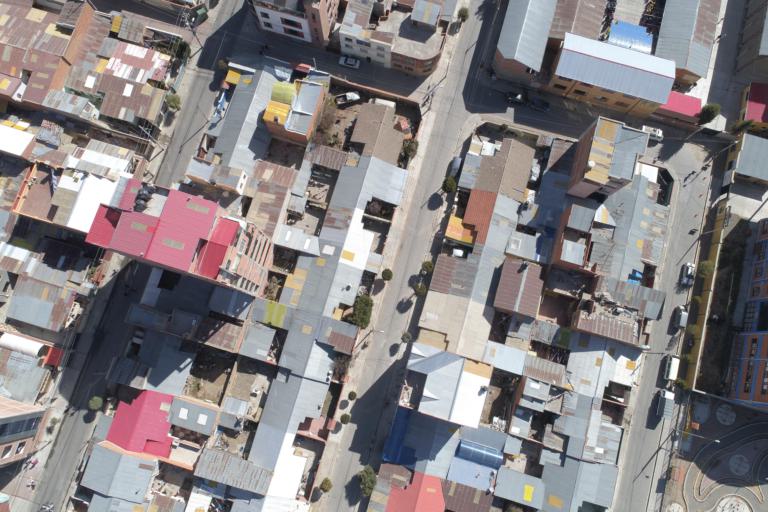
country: BO
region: La Paz
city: La Paz
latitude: -16.5275
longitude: -68.1550
